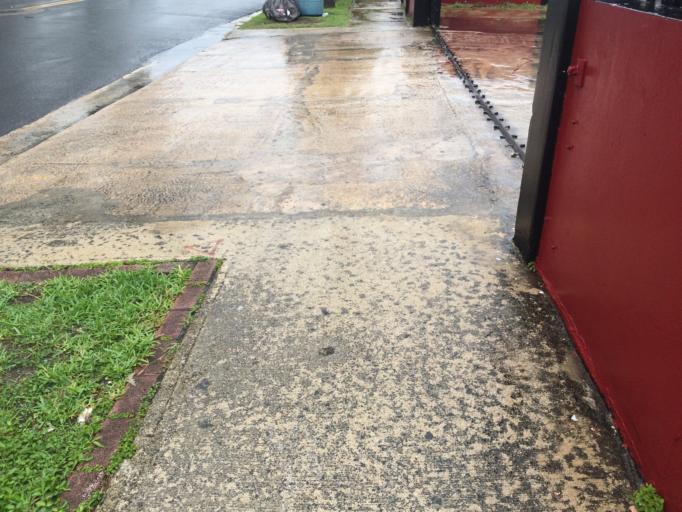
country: PR
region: Catano
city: Catano
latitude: 18.4162
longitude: -66.0569
